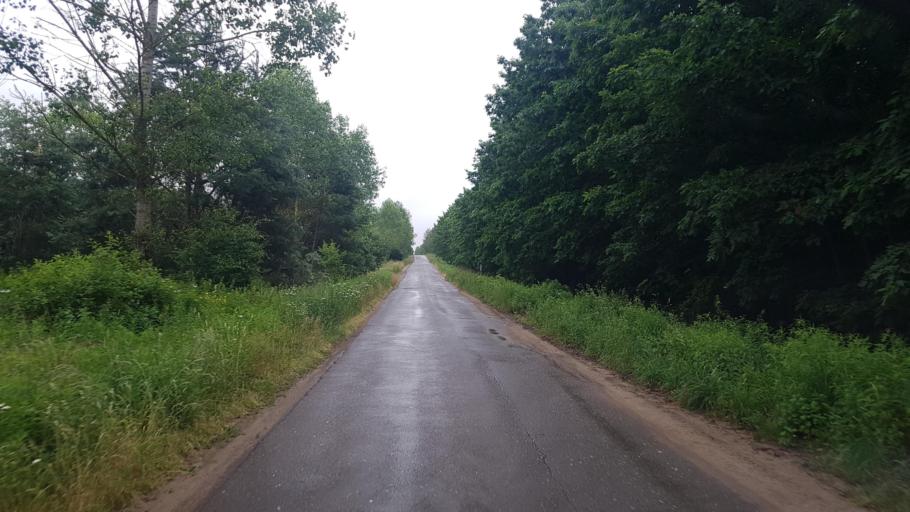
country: DE
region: Brandenburg
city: Lauchhammer
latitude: 51.5421
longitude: 13.7496
